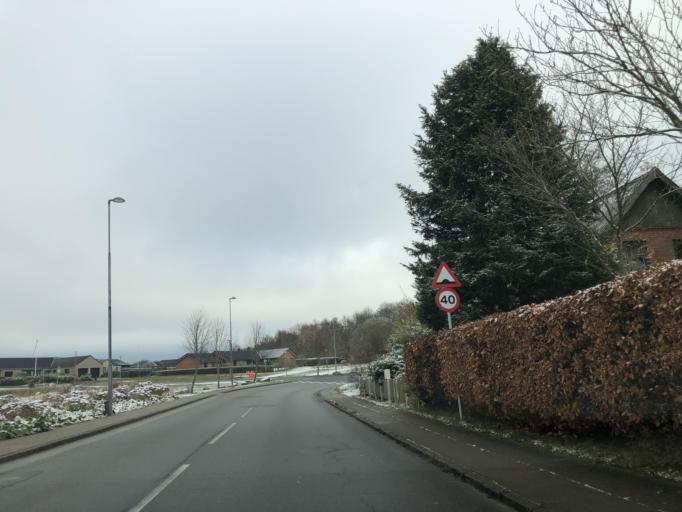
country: DK
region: South Denmark
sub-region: Vejle Kommune
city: Give
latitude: 55.9831
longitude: 9.2975
